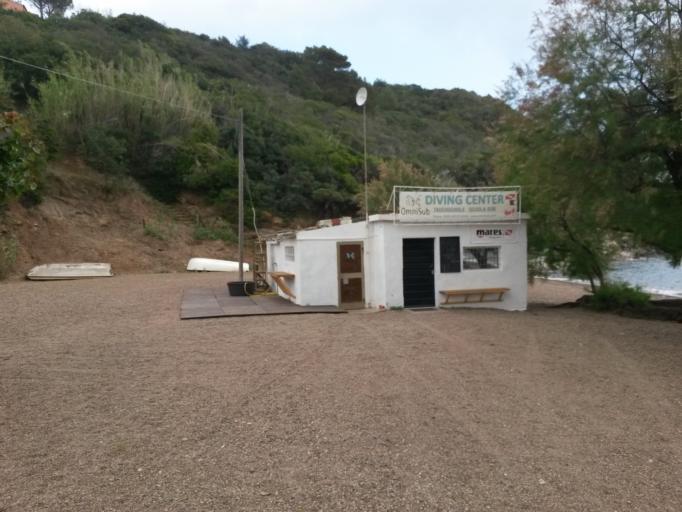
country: IT
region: Tuscany
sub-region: Provincia di Livorno
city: Porto Azzurro
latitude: 42.7696
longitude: 10.4079
